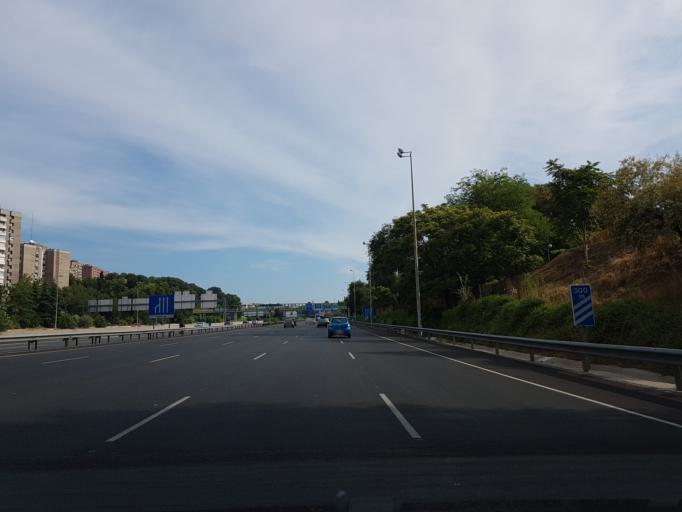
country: ES
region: Madrid
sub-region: Provincia de Madrid
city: Moratalaz
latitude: 40.4110
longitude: -3.6624
